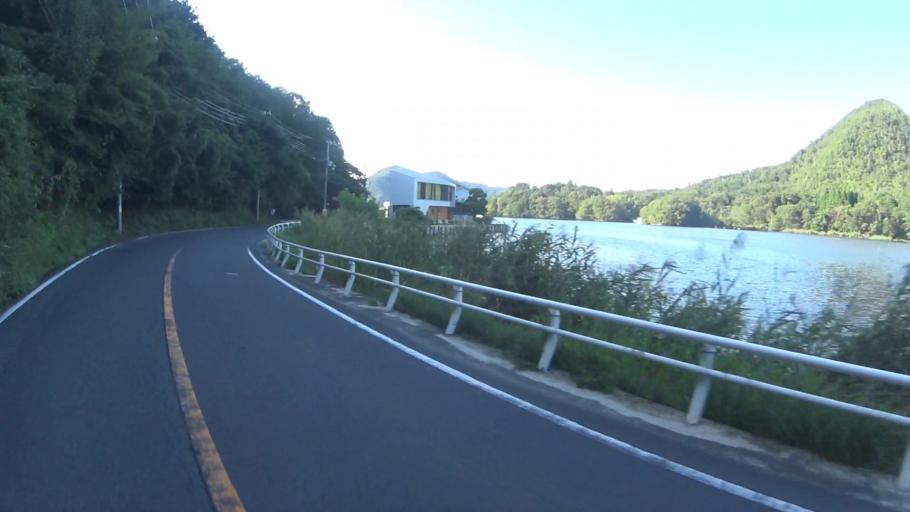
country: JP
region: Hyogo
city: Toyooka
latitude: 35.6053
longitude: 134.9082
